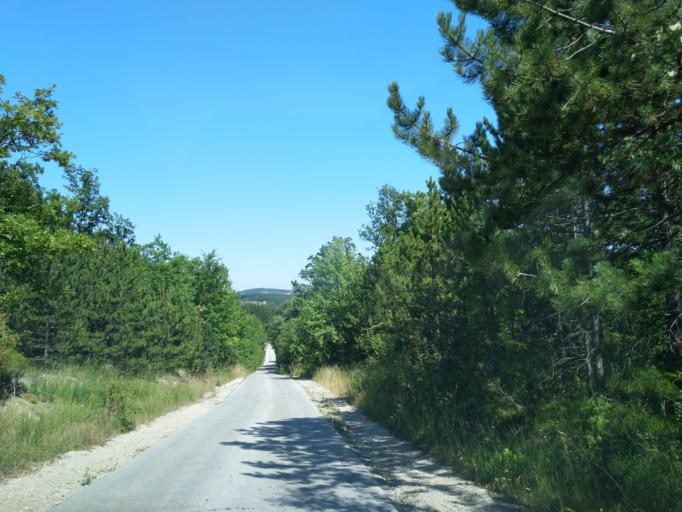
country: RS
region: Central Serbia
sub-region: Zlatiborski Okrug
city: Uzice
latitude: 43.8030
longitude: 19.8193
